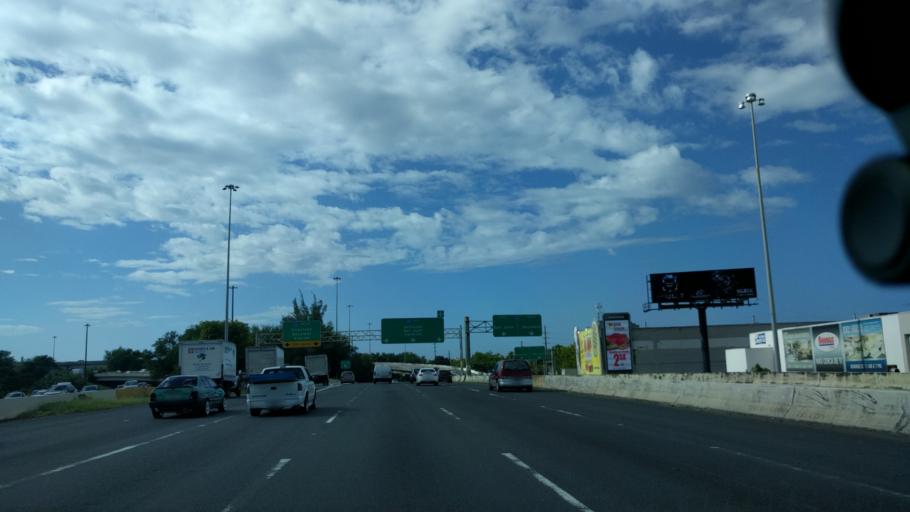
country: PR
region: Catano
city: Catano
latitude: 18.4257
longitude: -66.0729
